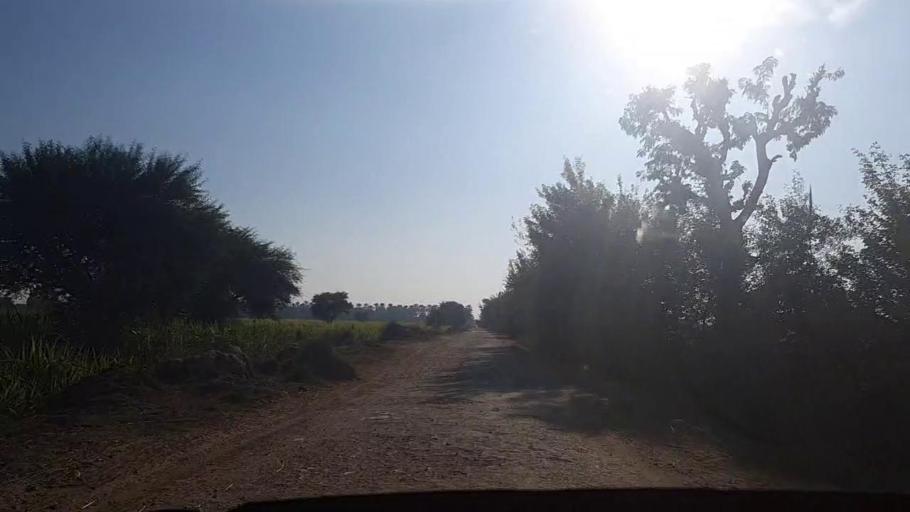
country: PK
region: Sindh
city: Gambat
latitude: 27.3586
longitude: 68.4562
